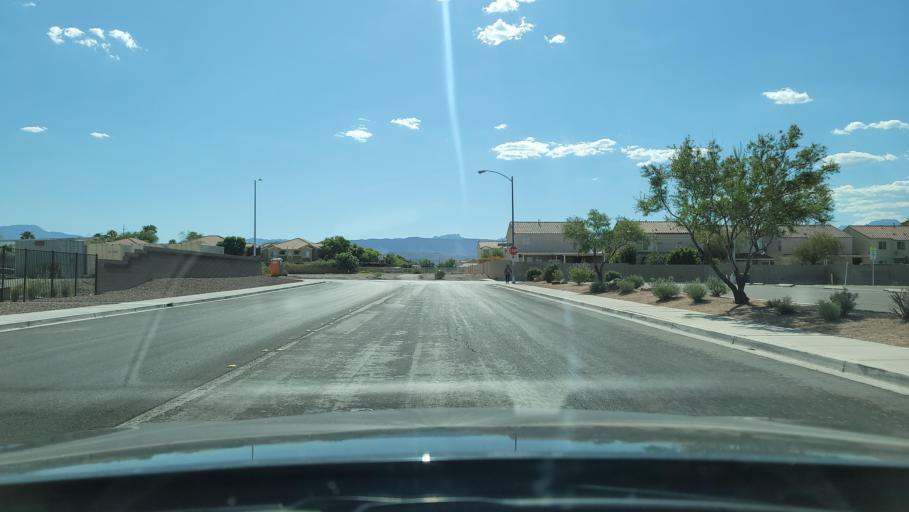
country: US
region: Nevada
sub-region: Clark County
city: Spring Valley
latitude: 36.0870
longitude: -115.2477
